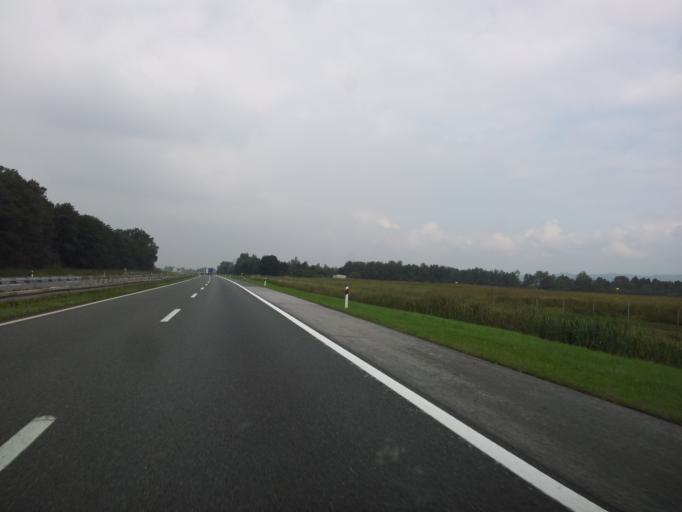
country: HR
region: Sisacko-Moslavacka
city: Repusnica
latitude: 45.4709
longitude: 16.7409
